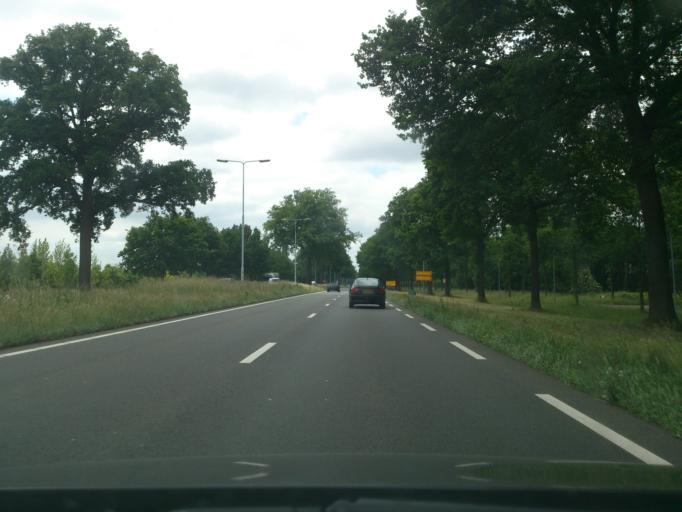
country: NL
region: North Brabant
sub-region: Gemeente Haaren
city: Haaren
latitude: 51.6076
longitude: 5.1950
